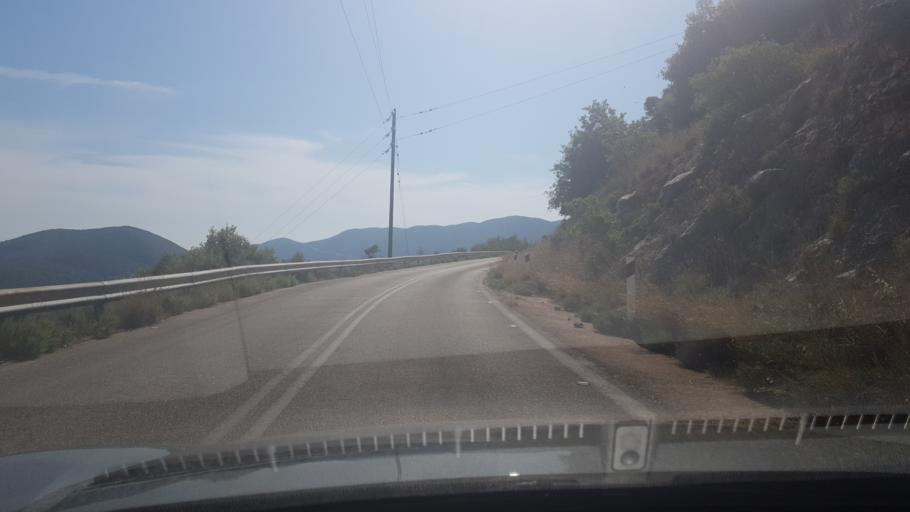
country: GR
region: Ionian Islands
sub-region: Lefkada
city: Nidri
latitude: 38.6499
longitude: 20.6624
